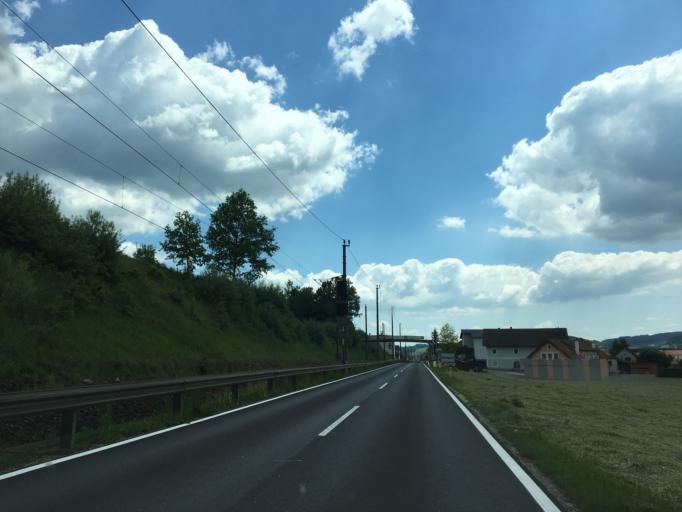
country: AT
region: Upper Austria
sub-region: Politischer Bezirk Freistadt
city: Freistadt
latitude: 48.4446
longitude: 14.5346
